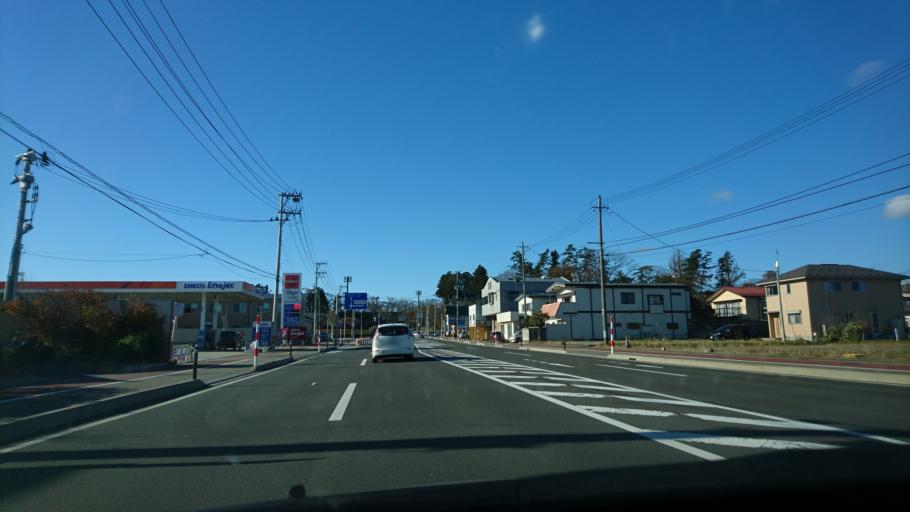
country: JP
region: Akita
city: Akita Shi
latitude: 39.3823
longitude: 140.0500
